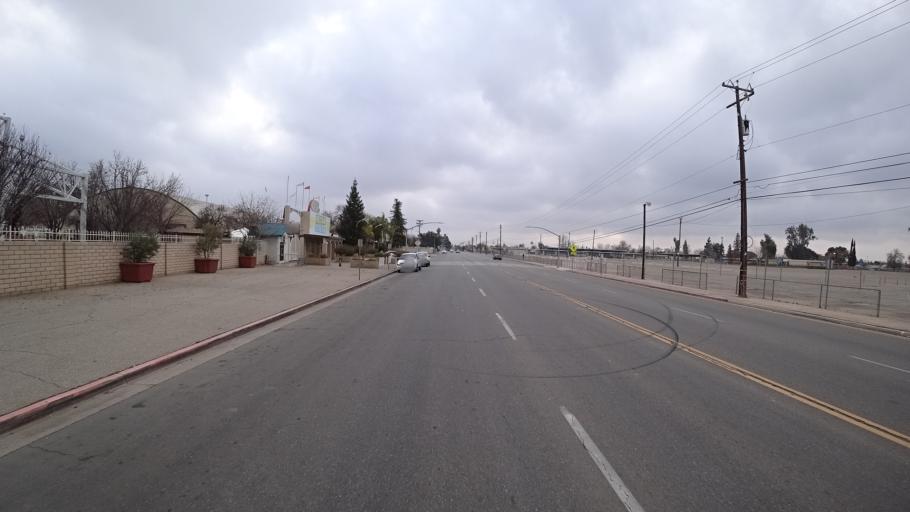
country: US
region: California
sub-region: Kern County
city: Bakersfield
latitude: 35.3429
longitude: -119.0119
